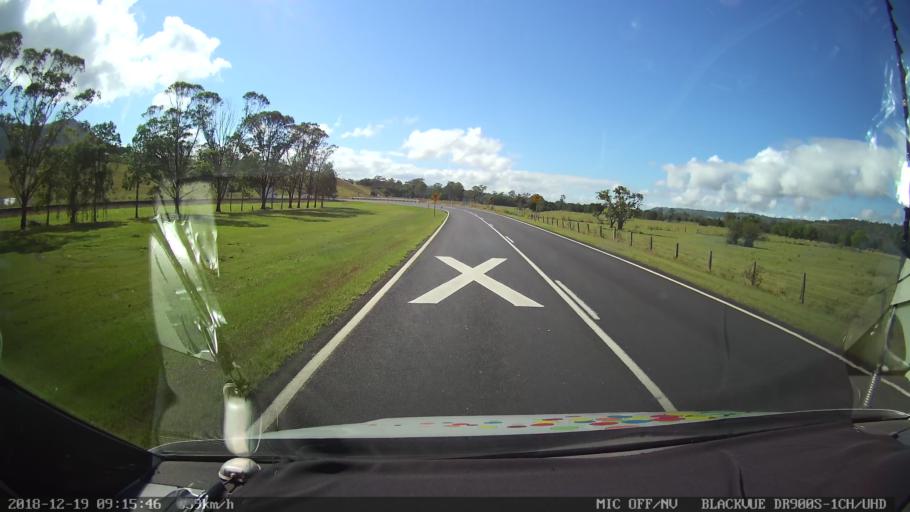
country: AU
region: New South Wales
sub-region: Kyogle
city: Kyogle
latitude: -28.5158
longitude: 152.9638
